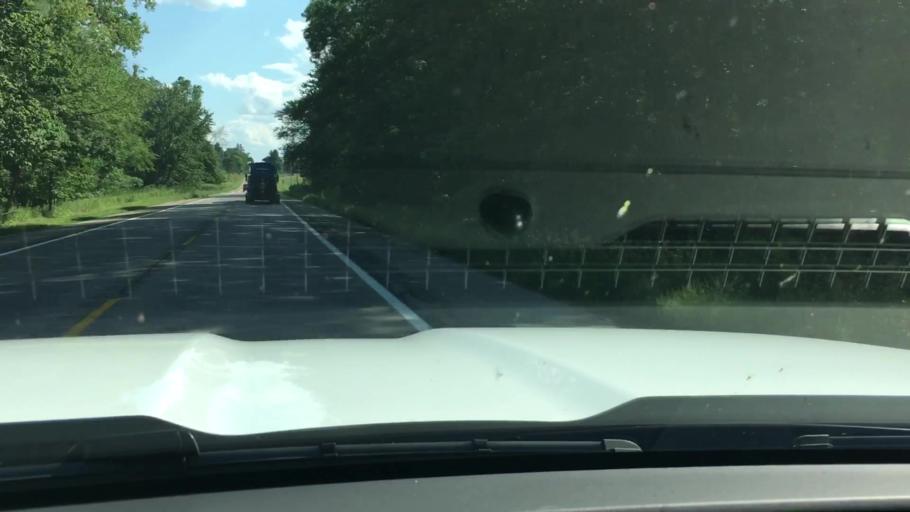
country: US
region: Michigan
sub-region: Ionia County
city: Ionia
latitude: 43.0623
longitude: -85.0752
